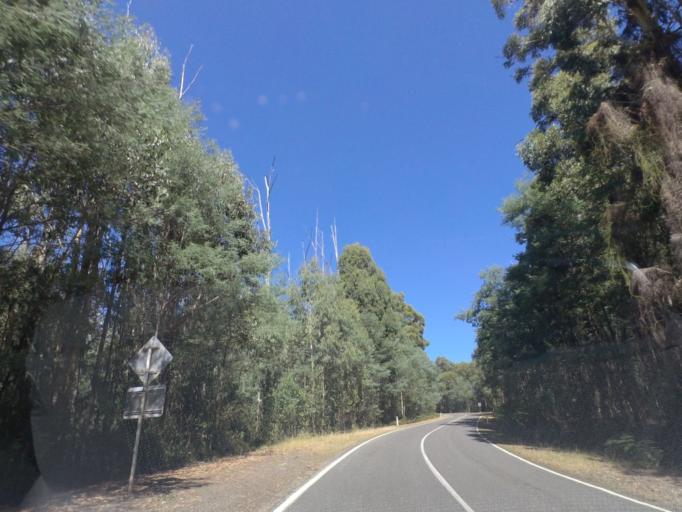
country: AU
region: Victoria
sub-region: Yarra Ranges
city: Millgrove
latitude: -37.5105
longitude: 145.7676
